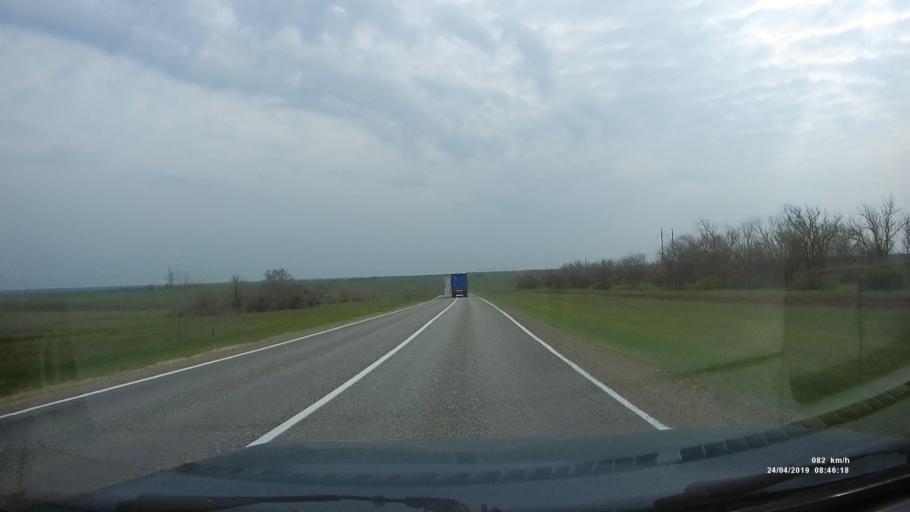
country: RU
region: Kalmykiya
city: Arshan'
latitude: 46.2382
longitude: 44.0765
